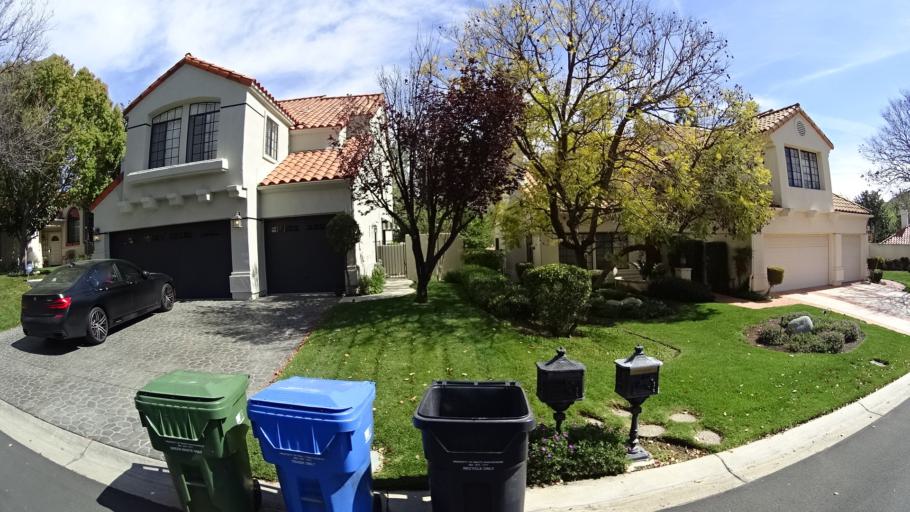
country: US
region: California
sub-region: Ventura County
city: Oak Park
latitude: 34.1755
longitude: -118.7895
